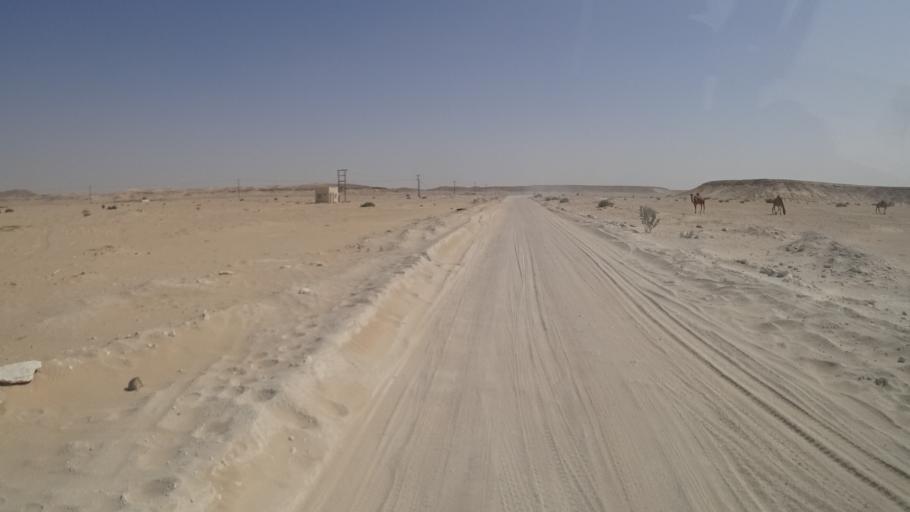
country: YE
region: Al Mahrah
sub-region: Shahan
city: Shihan as Sufla
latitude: 17.8733
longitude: 52.6081
